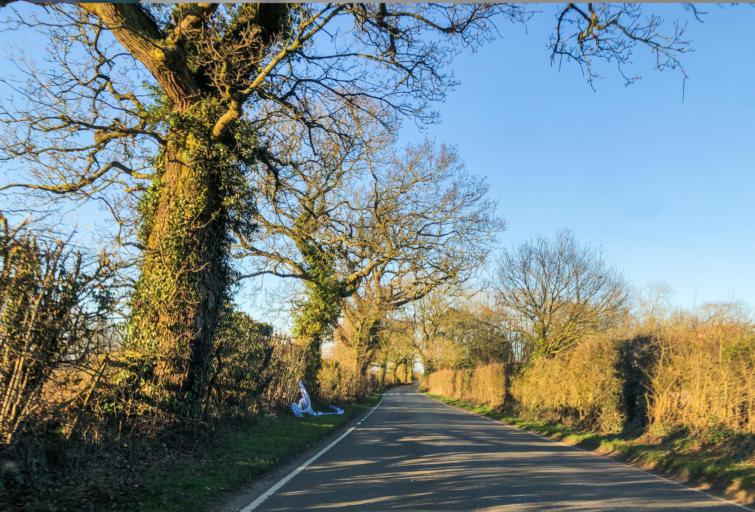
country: GB
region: England
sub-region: Warwickshire
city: Wroxall
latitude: 52.2900
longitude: -1.6601
